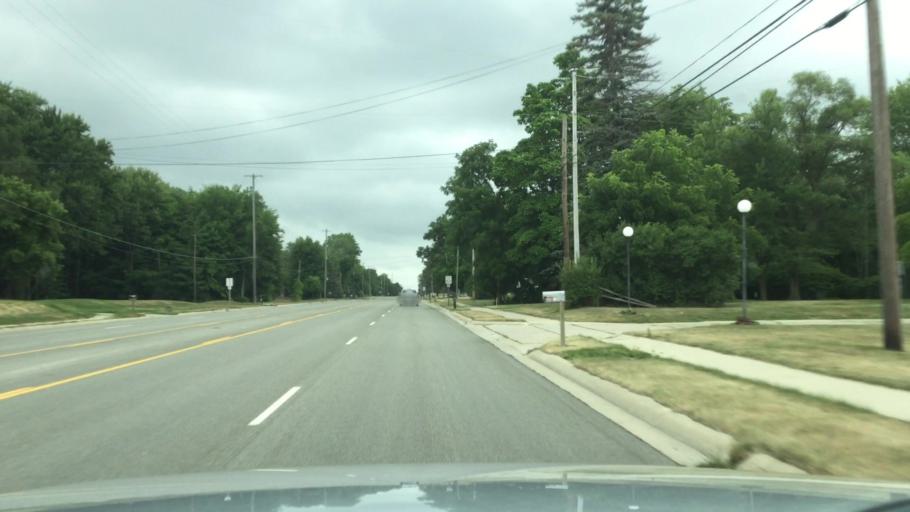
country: US
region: Michigan
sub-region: Genesee County
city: Davison
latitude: 43.0337
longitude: -83.5692
